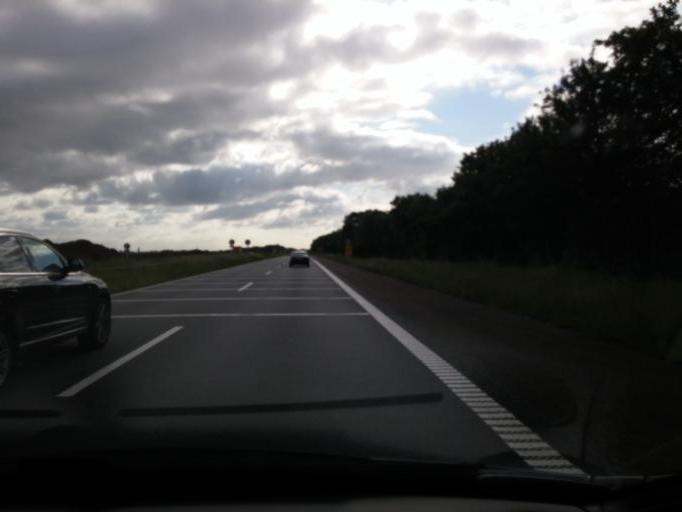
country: DK
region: Zealand
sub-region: Koge Kommune
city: Ejby
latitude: 55.4796
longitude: 12.1231
